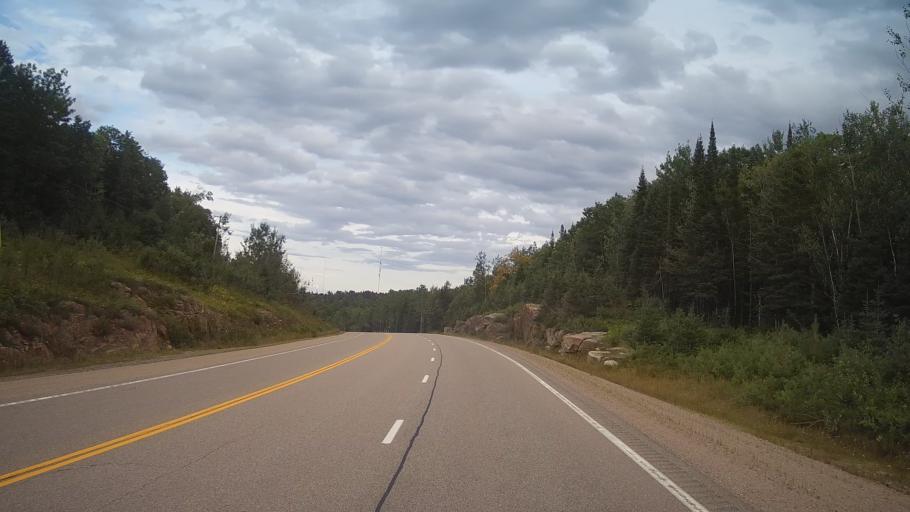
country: CA
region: Ontario
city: Mattawa
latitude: 46.2402
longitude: -78.1579
